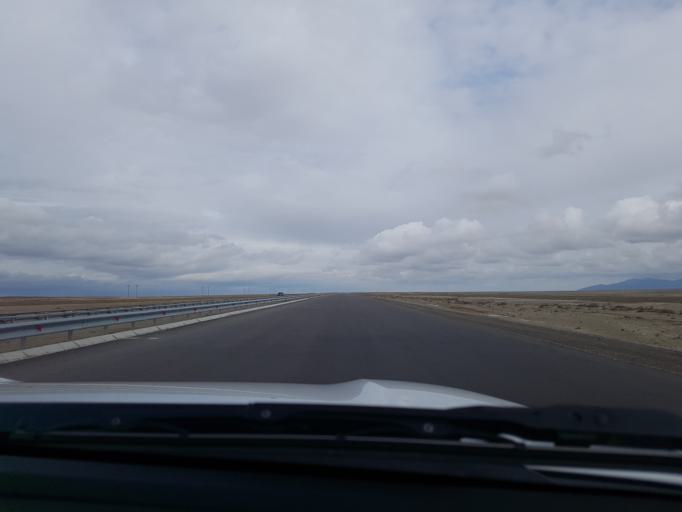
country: TM
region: Balkan
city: Gazanjyk
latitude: 39.2722
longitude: 55.1576
